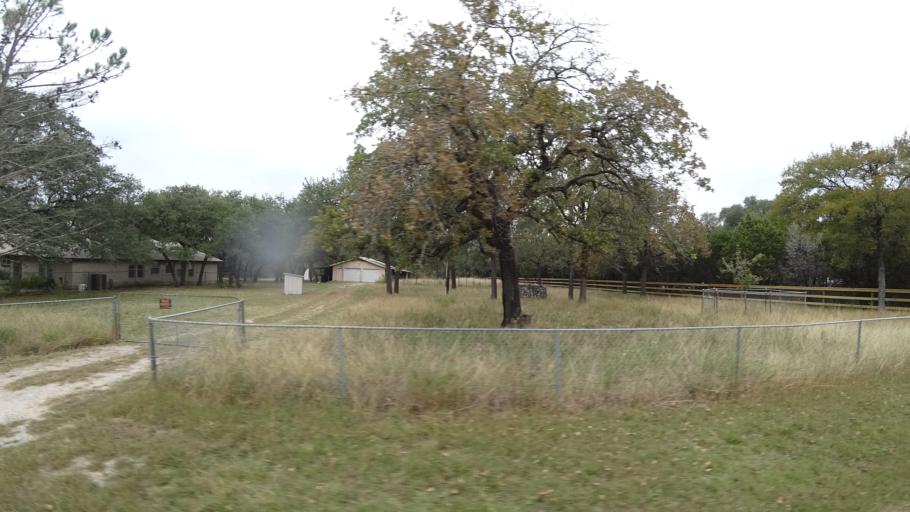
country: US
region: Texas
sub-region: Williamson County
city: Anderson Mill
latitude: 30.4512
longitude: -97.8347
